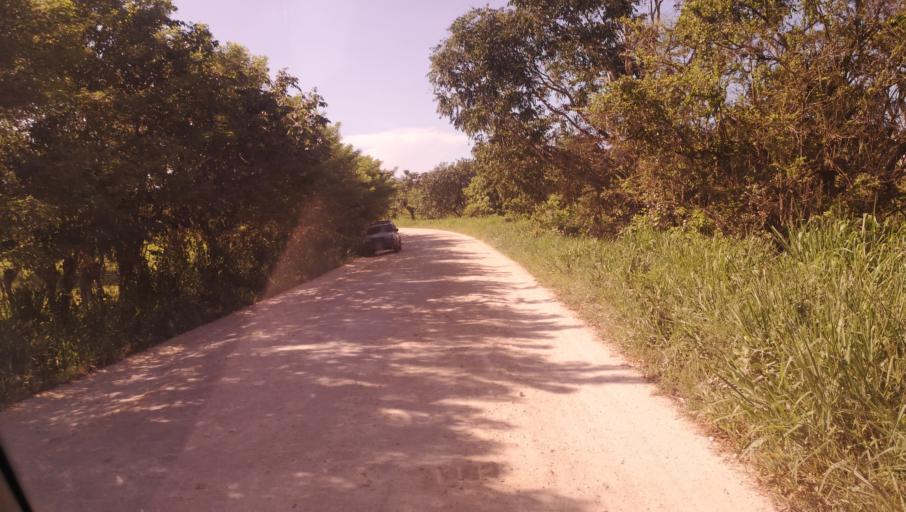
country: GT
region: Peten
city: Dolores
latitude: 16.7218
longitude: -89.3771
